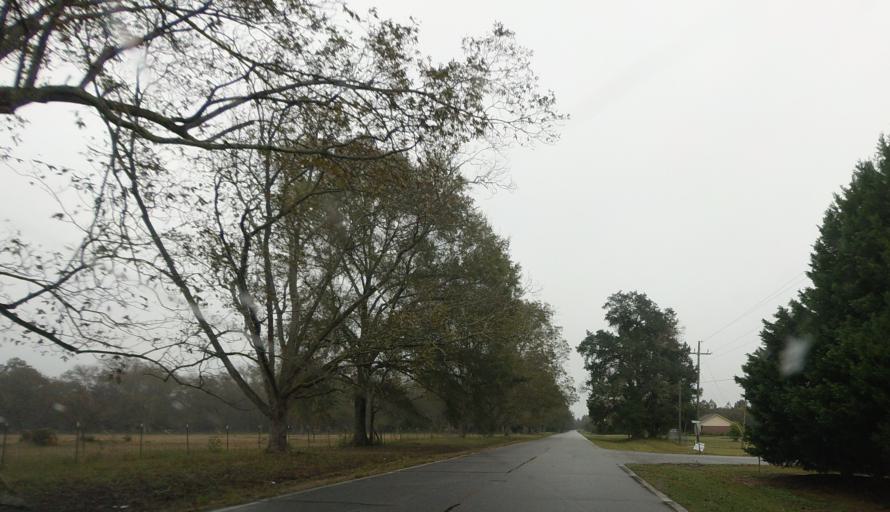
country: US
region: Georgia
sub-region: Peach County
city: Fort Valley
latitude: 32.5461
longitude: -83.9122
